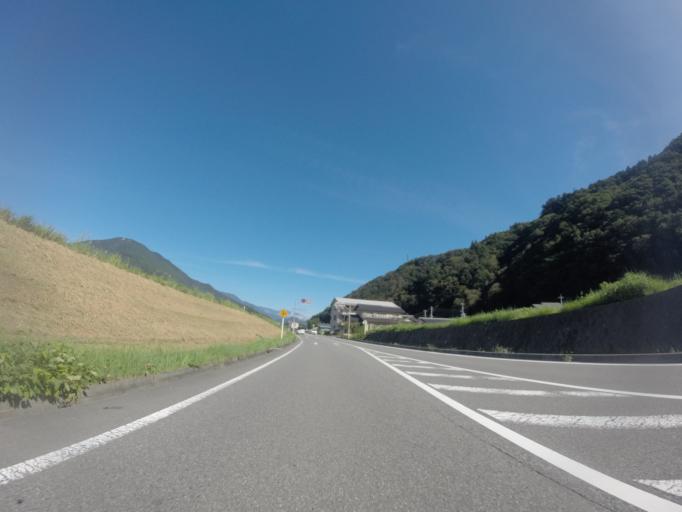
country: JP
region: Shizuoka
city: Fujinomiya
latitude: 35.3694
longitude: 138.4540
